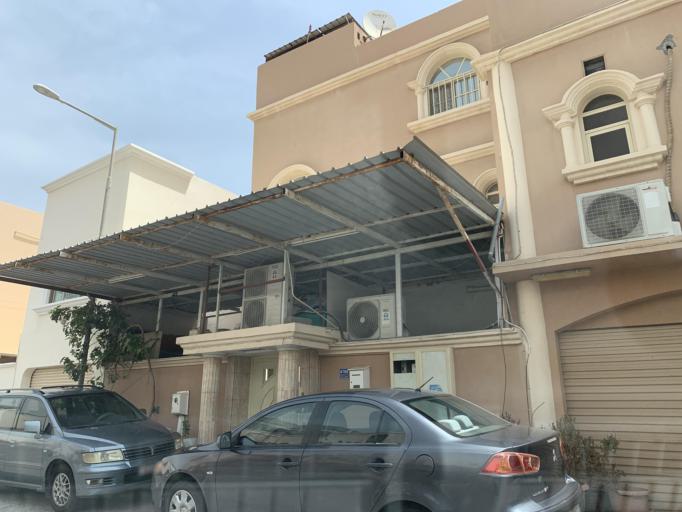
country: BH
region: Northern
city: Madinat `Isa
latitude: 26.1732
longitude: 50.5520
